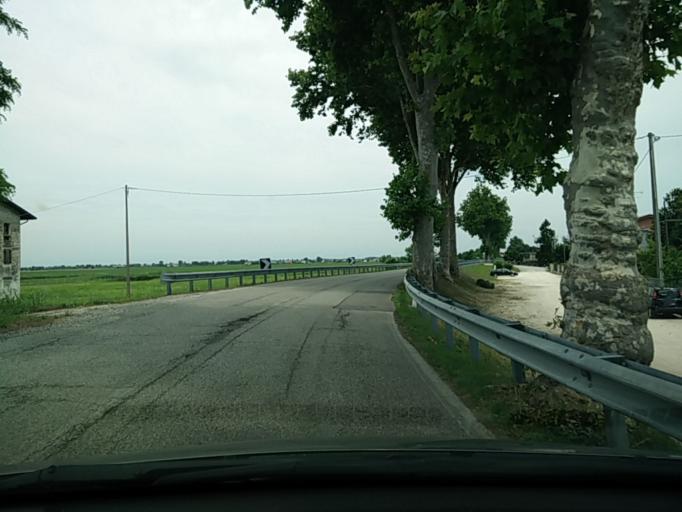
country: IT
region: Veneto
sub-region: Provincia di Venezia
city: Musile di Piave
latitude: 45.5823
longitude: 12.5466
